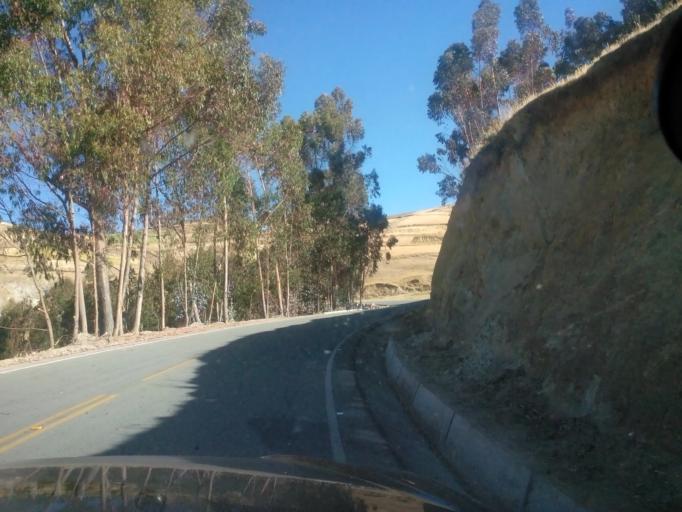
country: PE
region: Apurimac
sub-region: Provincia de Andahuaylas
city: Pacucha
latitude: -13.6595
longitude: -73.2887
